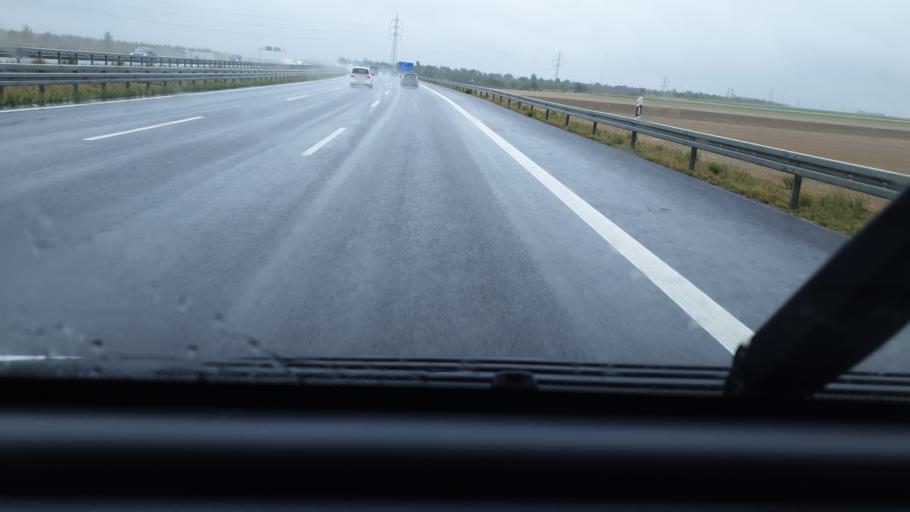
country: DE
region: North Rhine-Westphalia
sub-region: Regierungsbezirk Dusseldorf
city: Juchen
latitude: 51.0381
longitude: 6.4916
